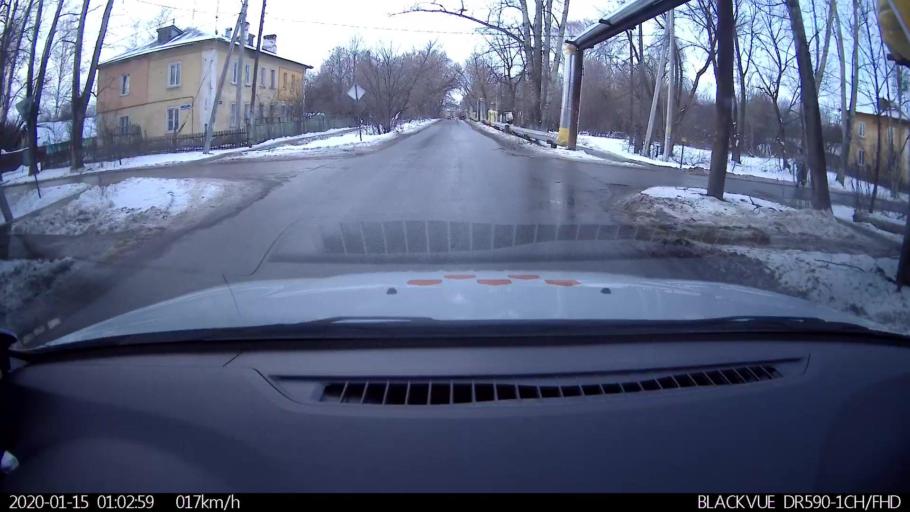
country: RU
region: Nizjnij Novgorod
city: Gorbatovka
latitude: 56.2273
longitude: 43.8380
